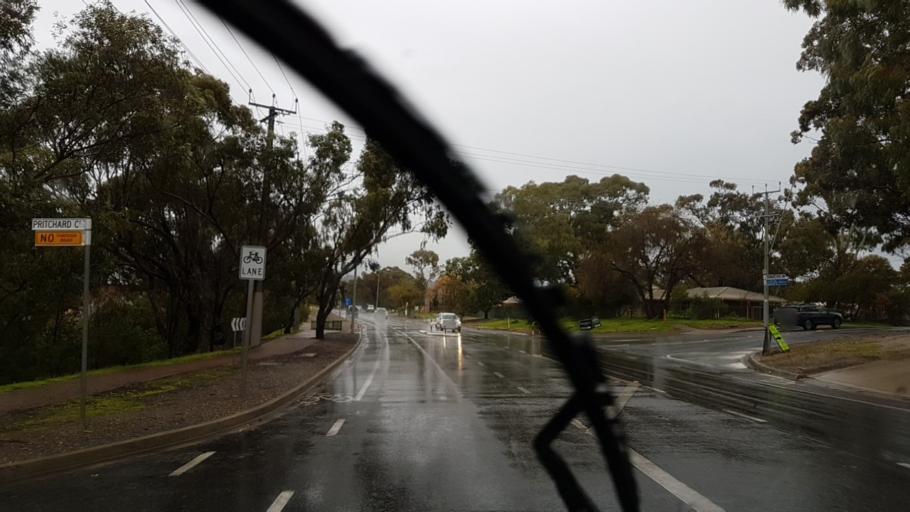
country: AU
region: South Australia
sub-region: Onkaparinga
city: Craigburn Farm
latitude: -35.0559
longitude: 138.5974
